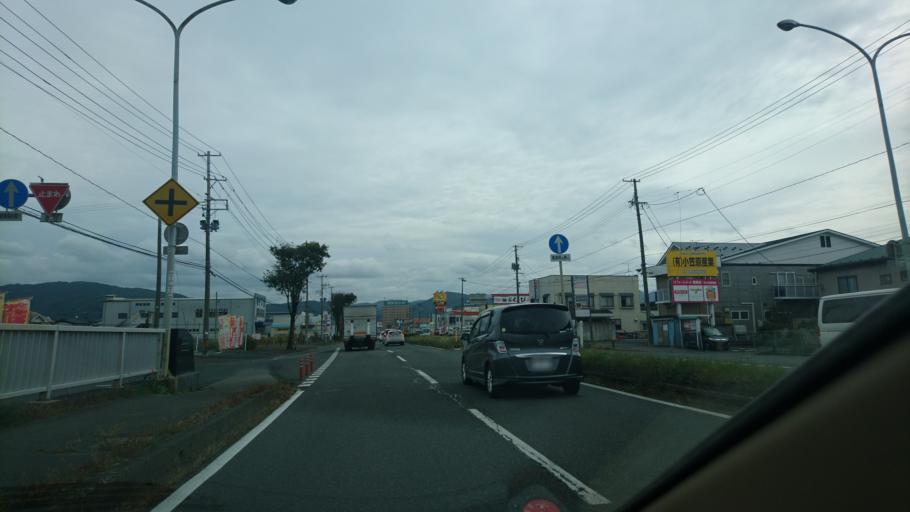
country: JP
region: Iwate
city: Morioka-shi
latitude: 39.6570
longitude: 141.1512
